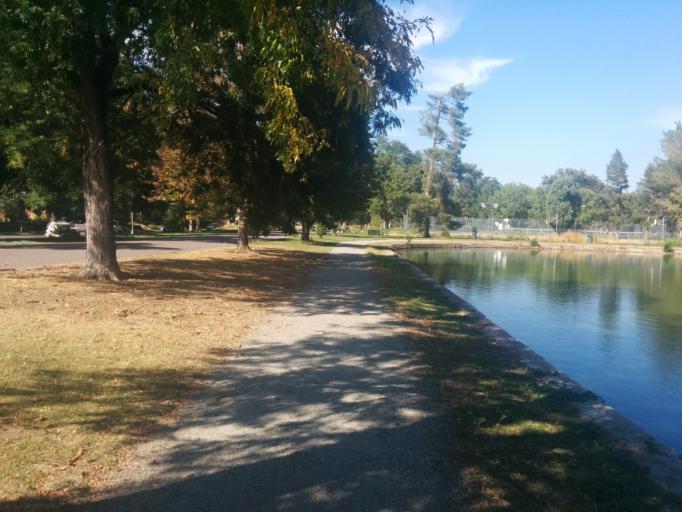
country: US
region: Colorado
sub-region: Arapahoe County
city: Glendale
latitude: 39.6970
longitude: -104.9727
